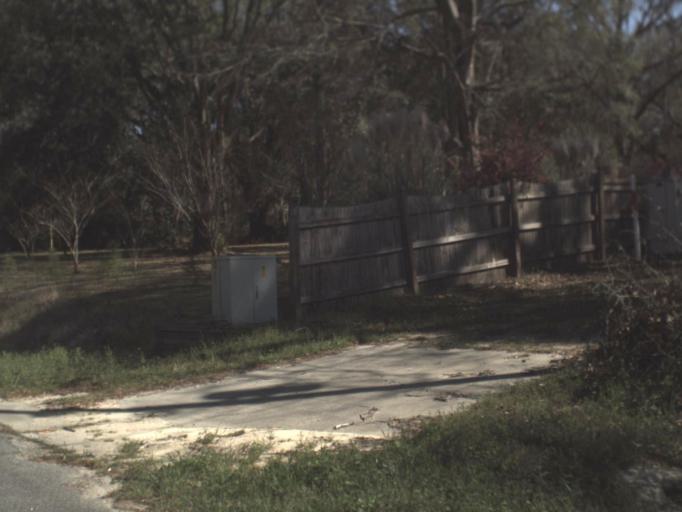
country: US
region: Florida
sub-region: Jefferson County
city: Monticello
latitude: 30.5066
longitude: -84.0243
